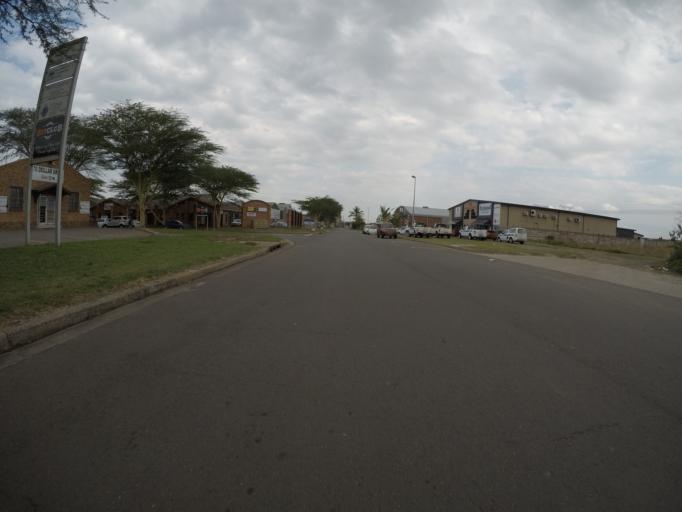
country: ZA
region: KwaZulu-Natal
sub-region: uThungulu District Municipality
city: Richards Bay
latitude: -28.7582
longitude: 32.0423
